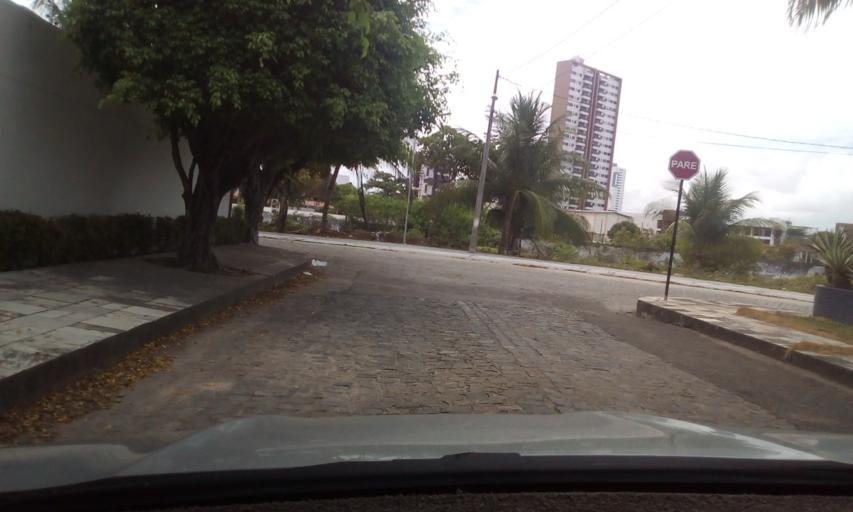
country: BR
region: Paraiba
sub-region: Joao Pessoa
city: Joao Pessoa
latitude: -7.0777
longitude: -34.8346
